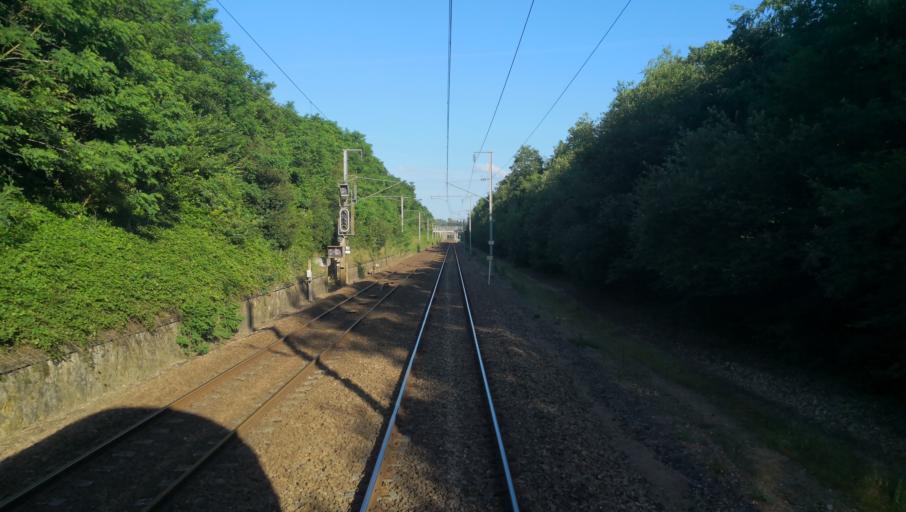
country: FR
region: Haute-Normandie
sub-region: Departement de l'Eure
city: Conches-en-Ouche
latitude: 48.9691
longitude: 0.9155
